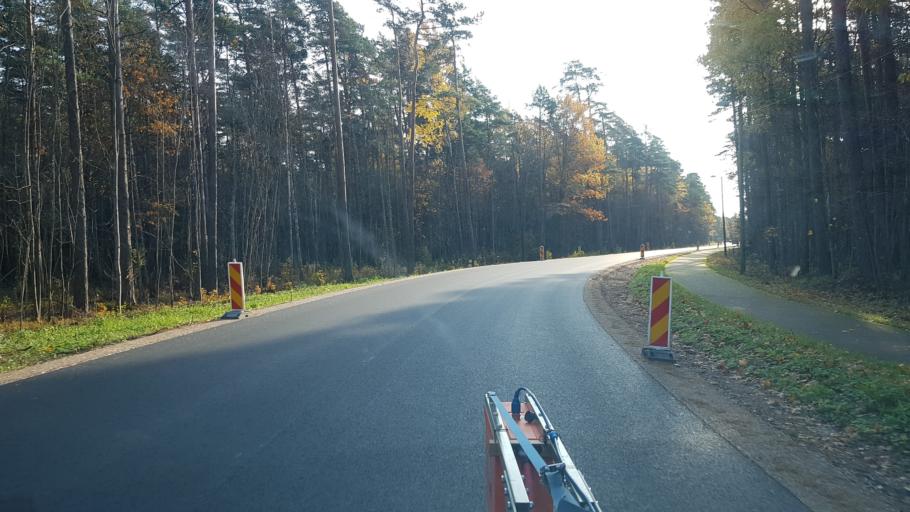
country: EE
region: Paernumaa
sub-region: Paikuse vald
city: Paikuse
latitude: 58.3666
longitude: 24.6009
